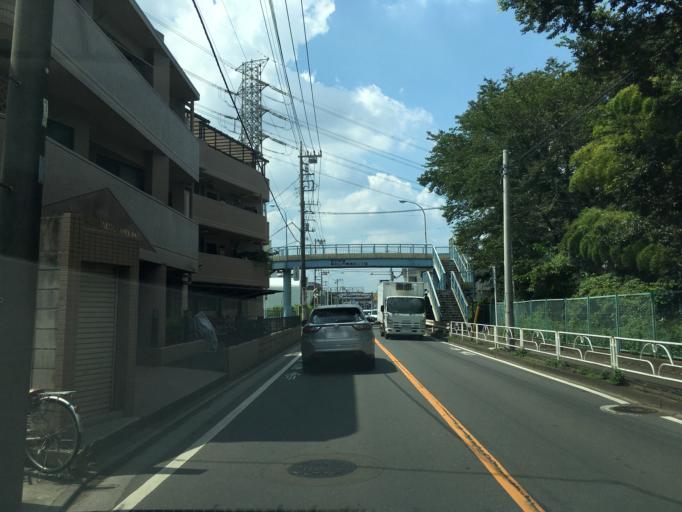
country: JP
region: Tokyo
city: Higashimurayama-shi
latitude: 35.7654
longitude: 139.4923
